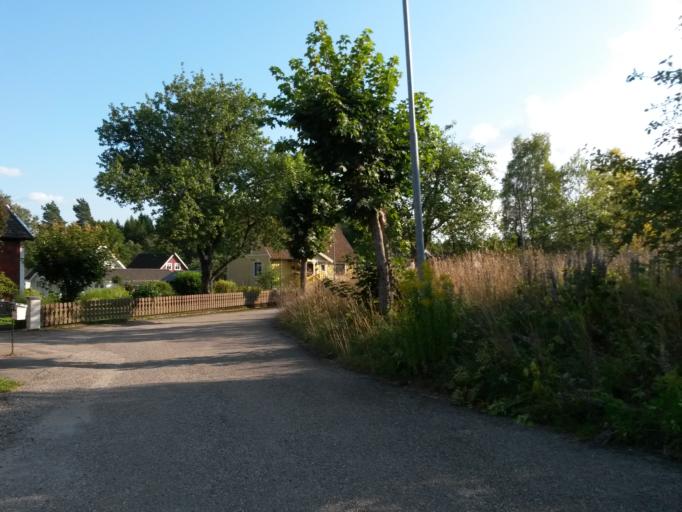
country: SE
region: Vaestra Goetaland
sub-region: Vargarda Kommun
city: Vargarda
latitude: 58.0345
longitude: 12.8240
